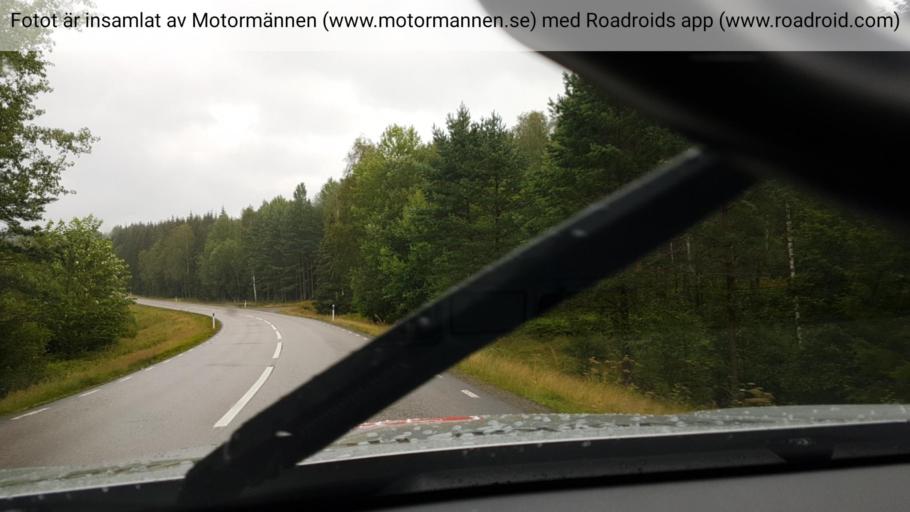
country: SE
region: Vaestra Goetaland
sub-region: Bengtsfors Kommun
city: Dals Langed
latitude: 58.8992
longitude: 12.2191
